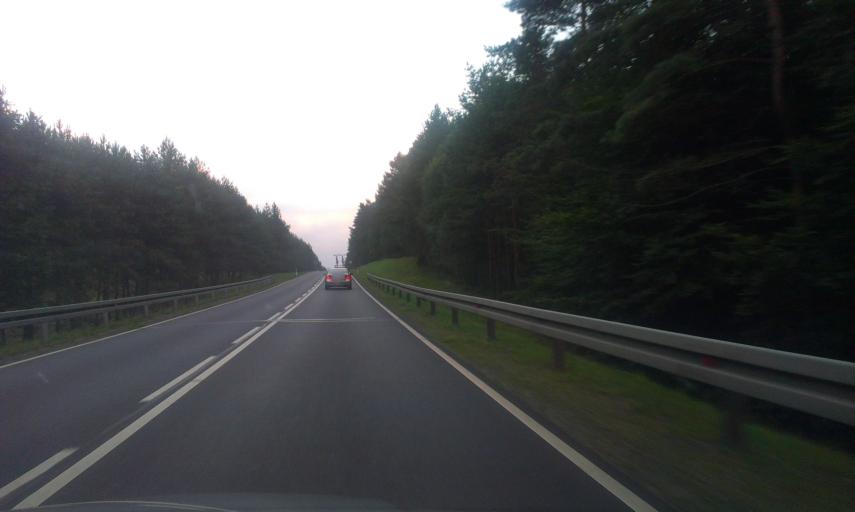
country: PL
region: West Pomeranian Voivodeship
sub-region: Powiat koszalinski
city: Sianow
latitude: 54.1056
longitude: 16.3399
